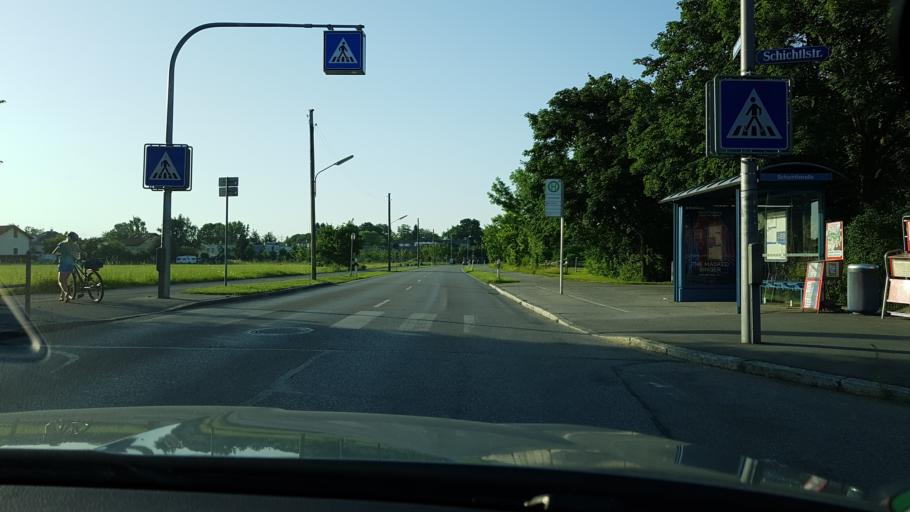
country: DE
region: Bavaria
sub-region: Upper Bavaria
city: Bogenhausen
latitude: 48.1470
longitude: 11.6585
